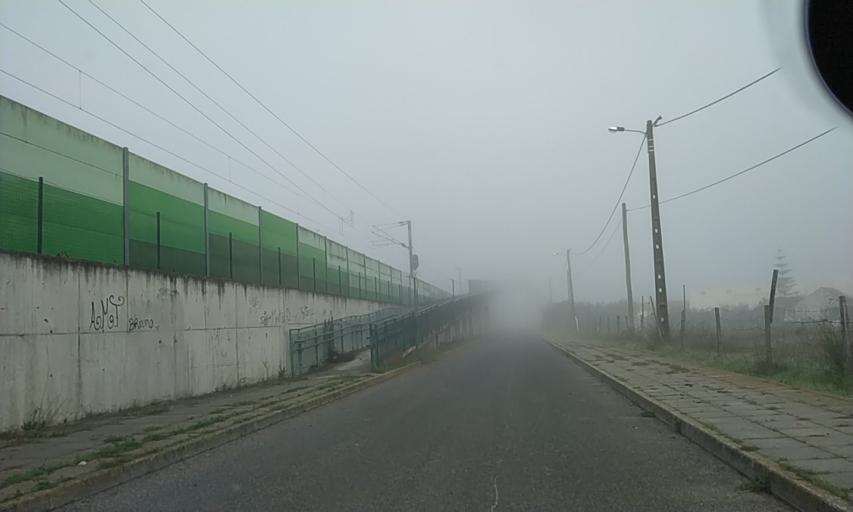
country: PT
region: Setubal
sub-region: Palmela
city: Pinhal Novo
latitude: 38.6075
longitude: -8.8894
